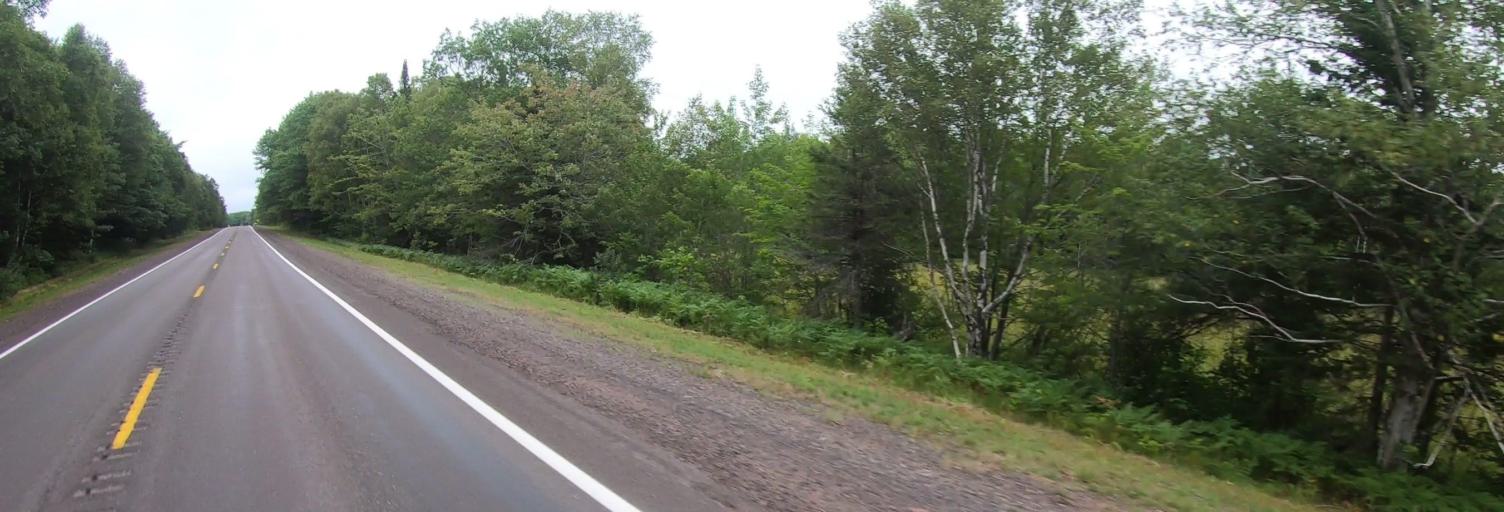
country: US
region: Michigan
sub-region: Keweenaw County
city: Eagle River
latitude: 47.3523
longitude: -88.3083
